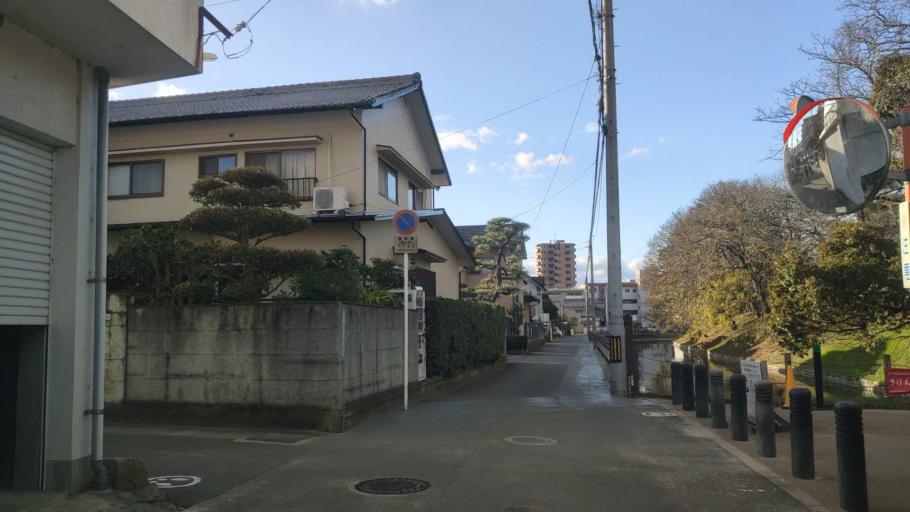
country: JP
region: Ehime
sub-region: Shikoku-chuo Shi
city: Matsuyama
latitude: 33.8485
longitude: 132.7884
